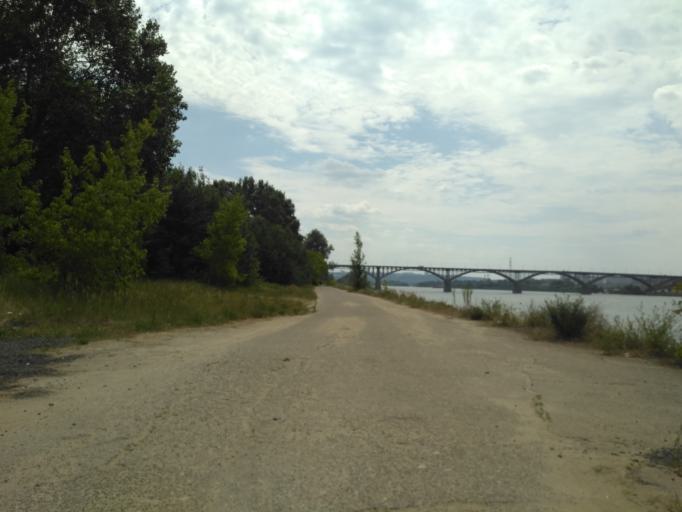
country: RU
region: Nizjnij Novgorod
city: Nizhniy Novgorod
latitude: 56.3089
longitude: 43.9681
